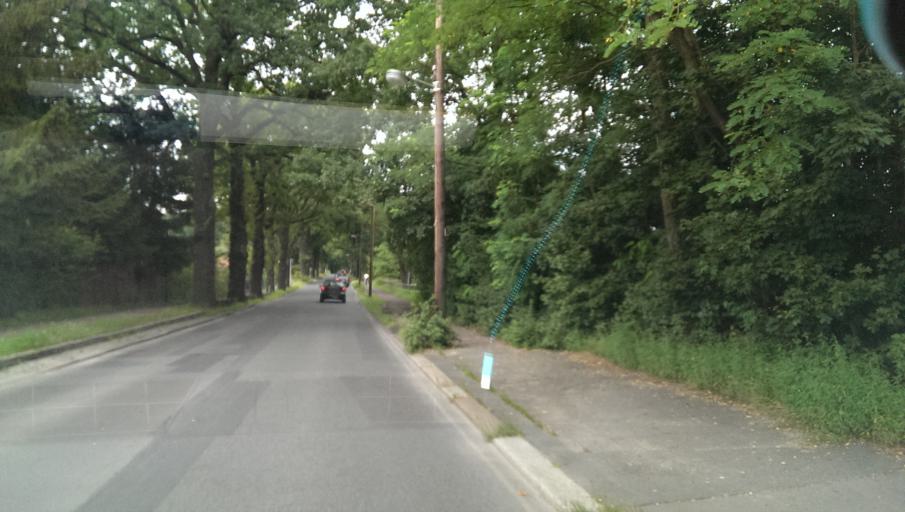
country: DE
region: Brandenburg
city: Kleinmachnow
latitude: 52.4213
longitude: 13.2251
